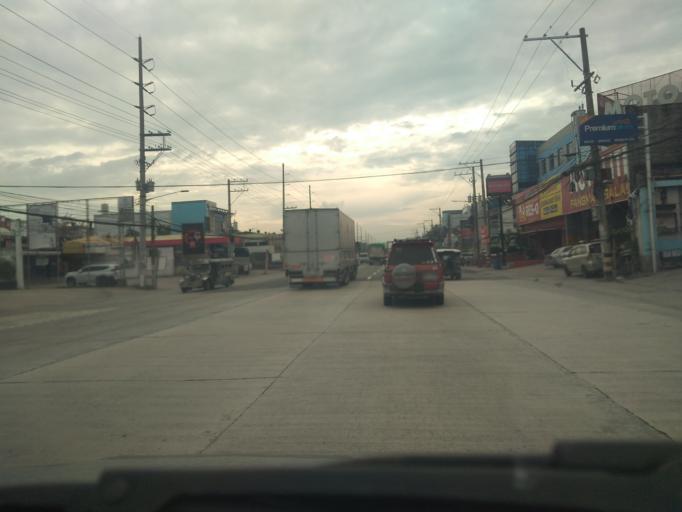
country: PH
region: Central Luzon
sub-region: Province of Pampanga
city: Magliman
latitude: 15.0441
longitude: 120.6736
